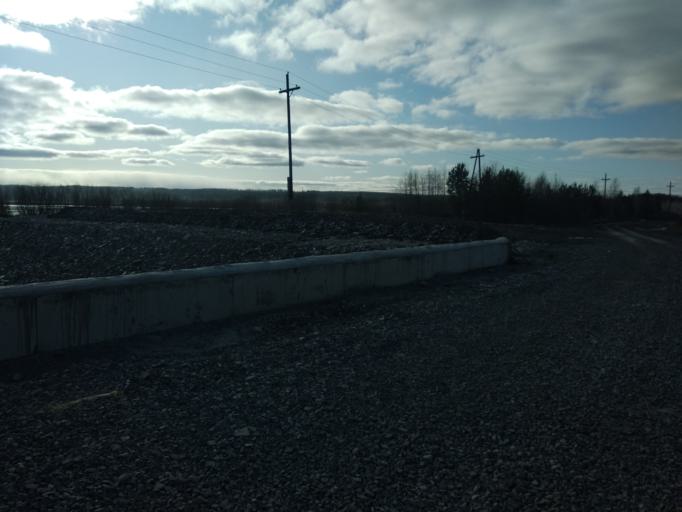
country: RU
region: Sverdlovsk
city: Karpinsk
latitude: 59.7523
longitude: 59.9757
